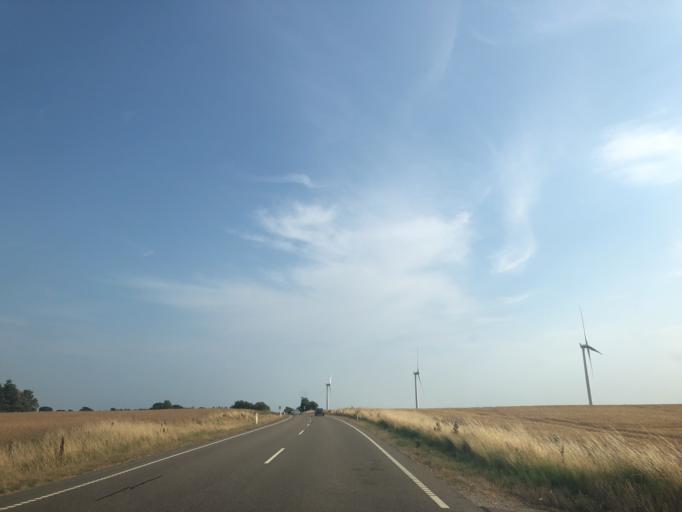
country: DK
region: North Denmark
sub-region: Morso Kommune
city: Nykobing Mors
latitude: 56.7717
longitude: 9.0358
